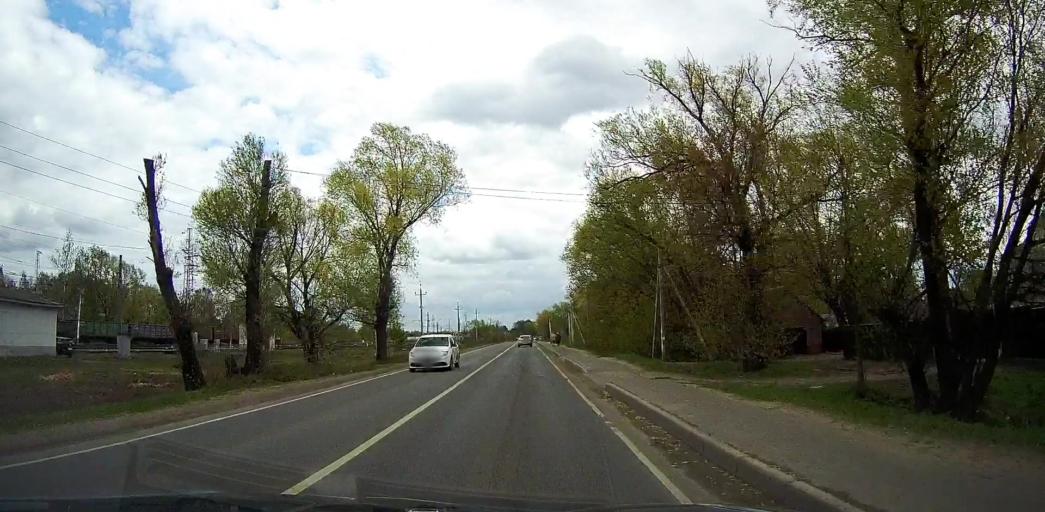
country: RU
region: Moskovskaya
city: Beloozerskiy
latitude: 55.4435
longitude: 38.4992
